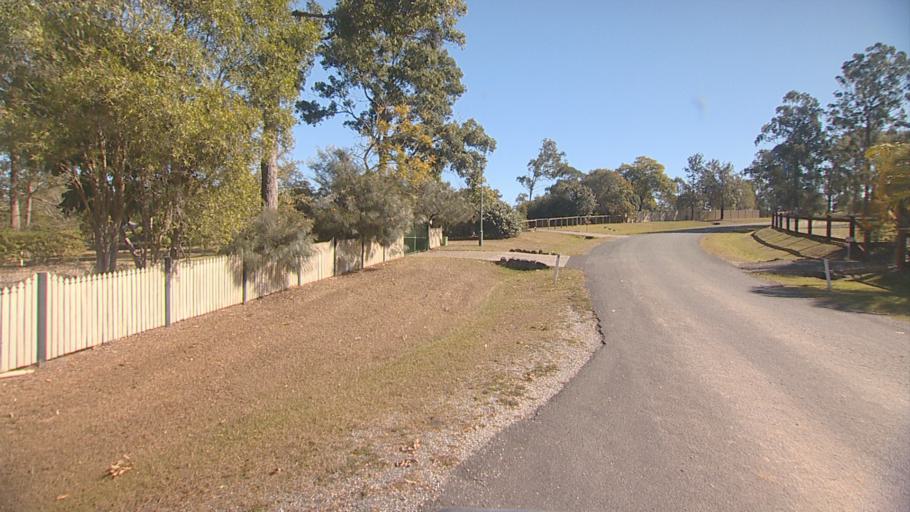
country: AU
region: Queensland
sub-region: Ipswich
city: Springfield Lakes
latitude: -27.7214
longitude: 152.9302
